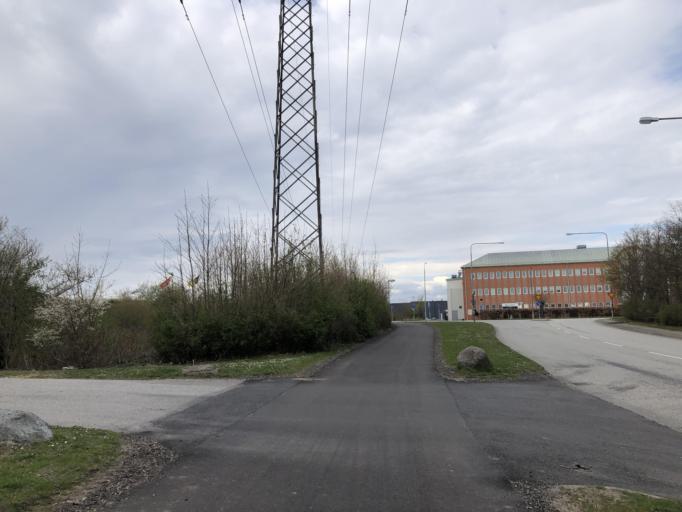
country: SE
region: Skane
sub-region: Malmo
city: Tygelsjo
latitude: 55.5537
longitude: 13.0447
